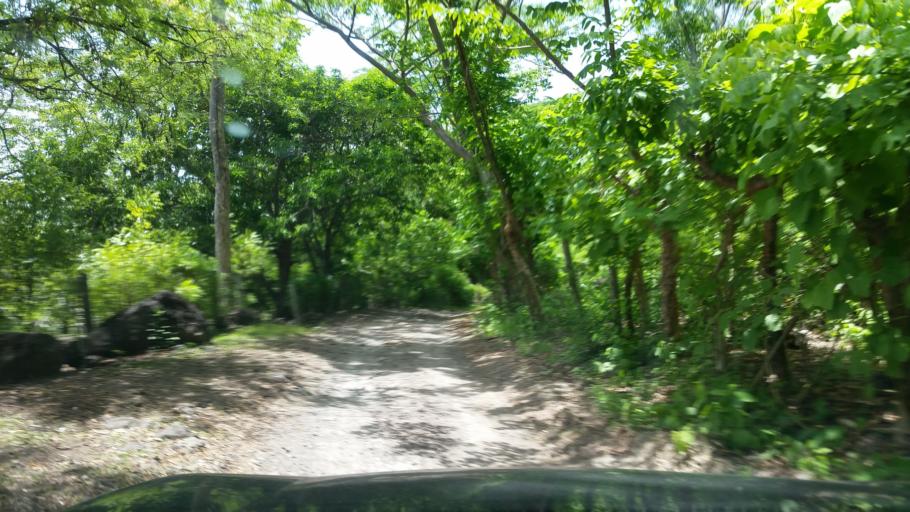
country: NI
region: Masaya
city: Catarina
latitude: 11.9121
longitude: -86.0571
